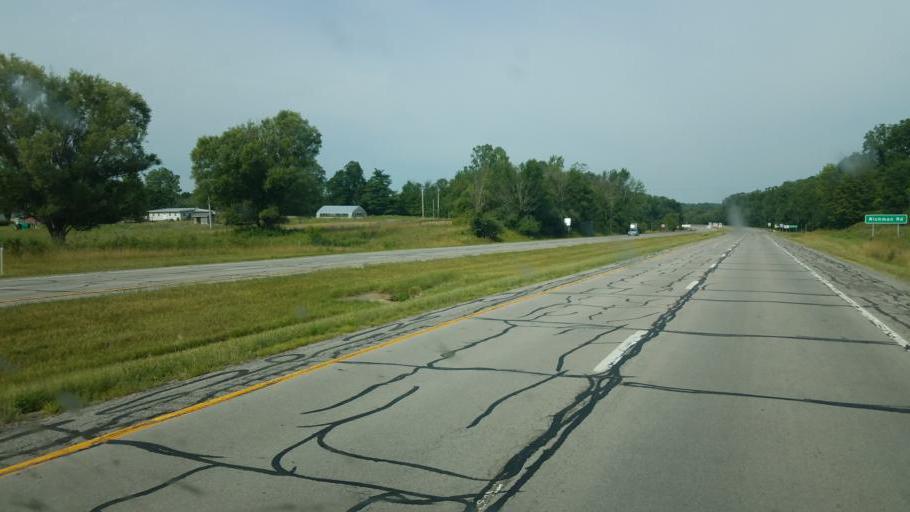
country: US
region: Ohio
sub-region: Medina County
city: Lodi
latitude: 41.0450
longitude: -82.0315
